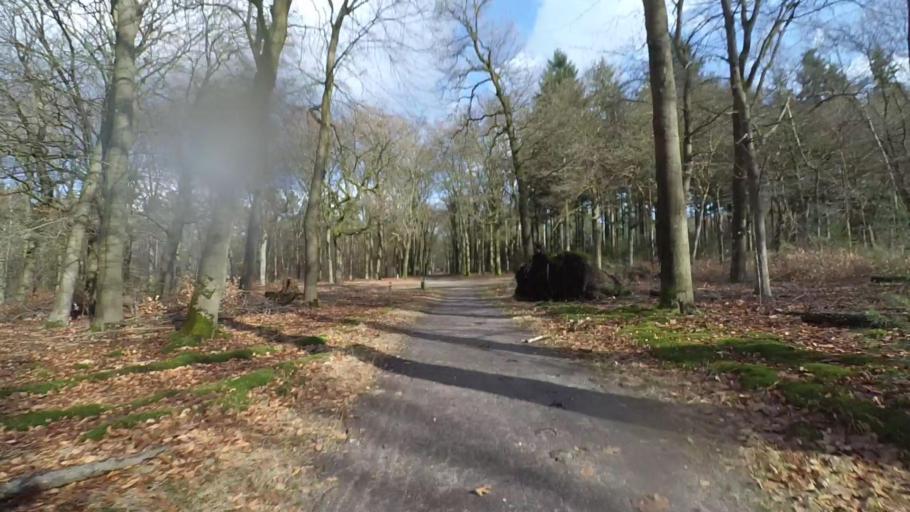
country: NL
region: Utrecht
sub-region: Gemeente Utrechtse Heuvelrug
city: Maarn
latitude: 52.0887
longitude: 5.3283
